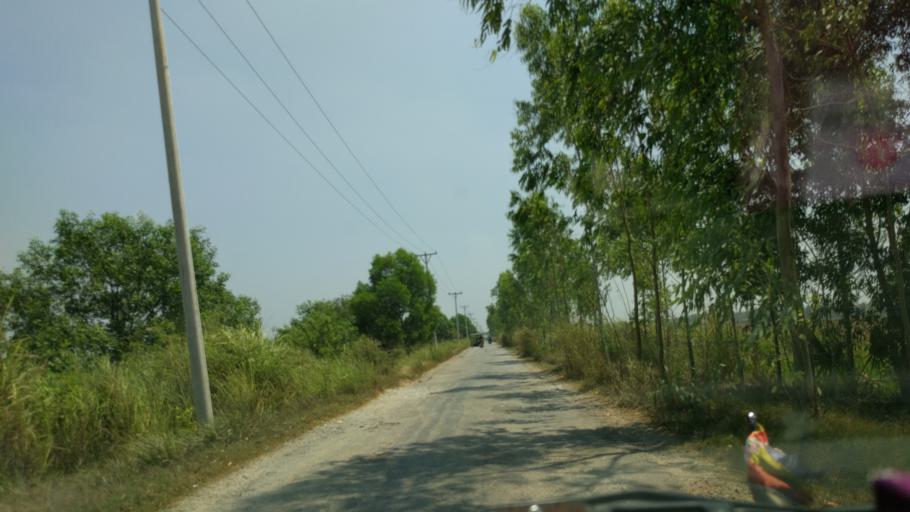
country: MM
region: Mon
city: Martaban
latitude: 16.5861
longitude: 97.6738
